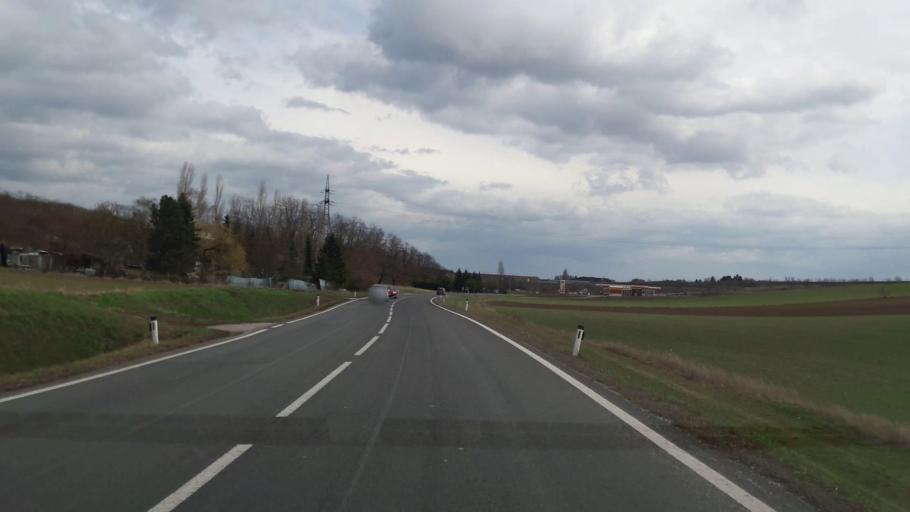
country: AT
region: Lower Austria
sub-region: Politischer Bezirk Mistelbach
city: Mistelbach
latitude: 48.5226
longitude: 16.6123
